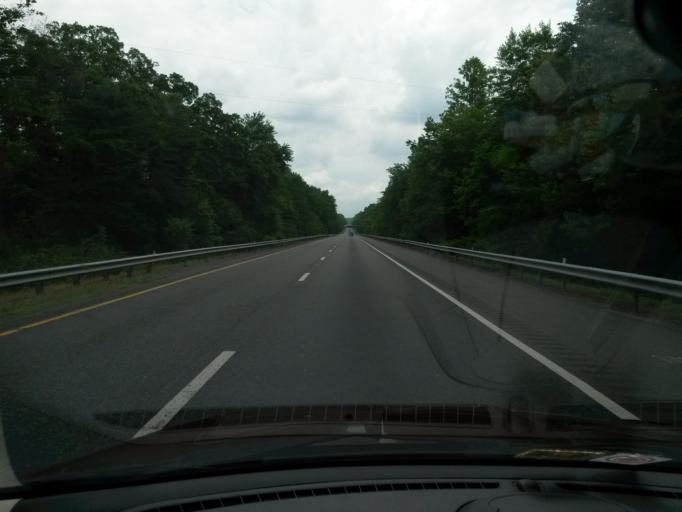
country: US
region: Virginia
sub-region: Fluvanna County
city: Lake Monticello
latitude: 38.0086
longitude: -78.3700
